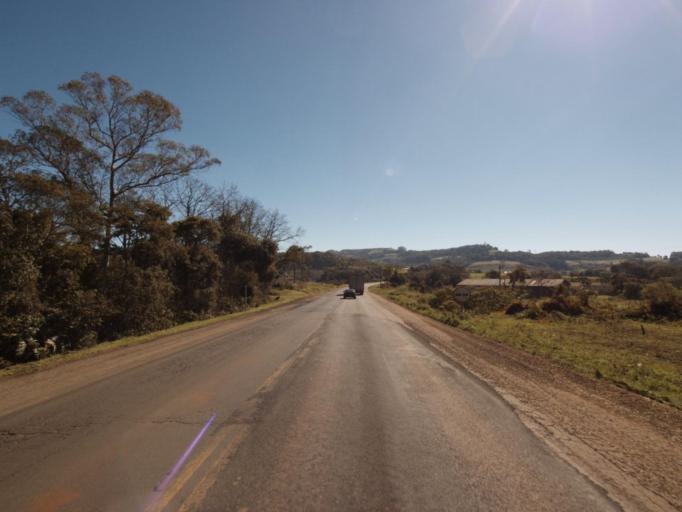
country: BR
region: Rio Grande do Sul
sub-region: Frederico Westphalen
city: Frederico Westphalen
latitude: -26.9027
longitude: -53.1890
